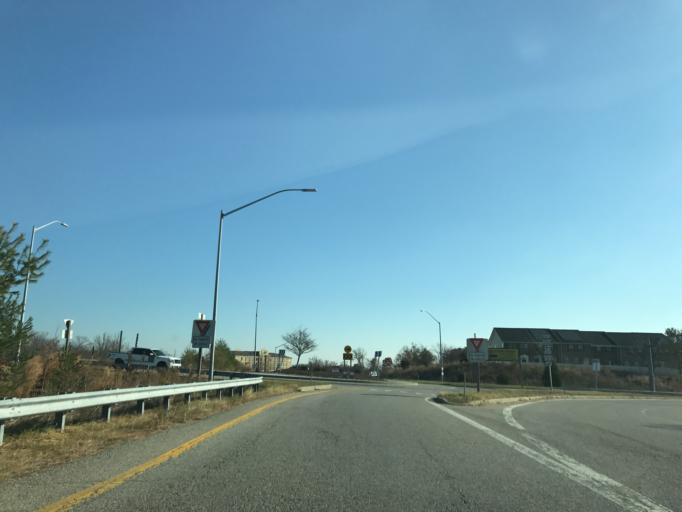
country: US
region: Maryland
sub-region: Howard County
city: Ilchester
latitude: 39.2074
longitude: -76.7832
